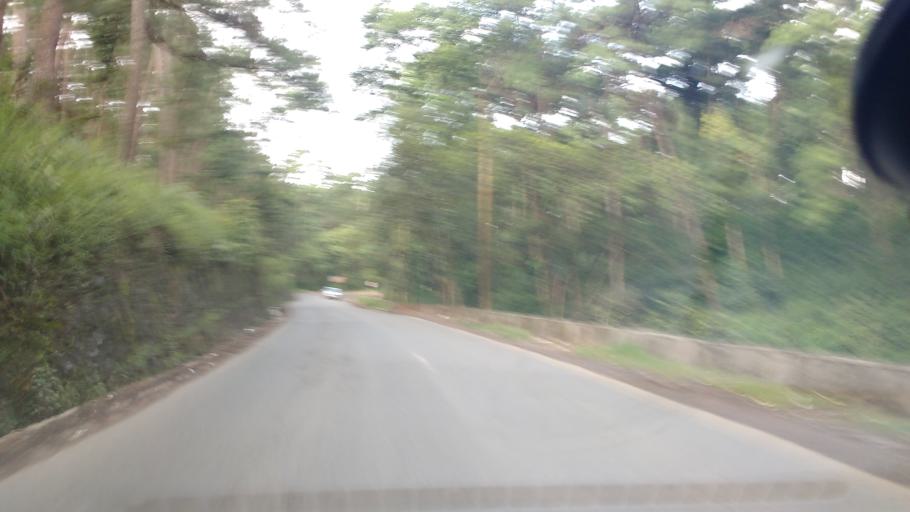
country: IN
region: Meghalaya
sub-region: East Khasi Hills
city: Shillong
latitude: 25.5665
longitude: 91.8575
